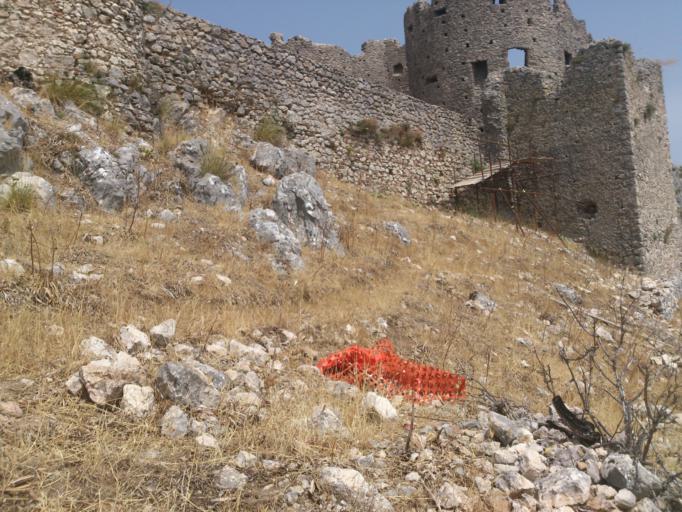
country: IT
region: Calabria
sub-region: Provincia di Reggio Calabria
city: Stilo
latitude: 38.4806
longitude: 16.4644
